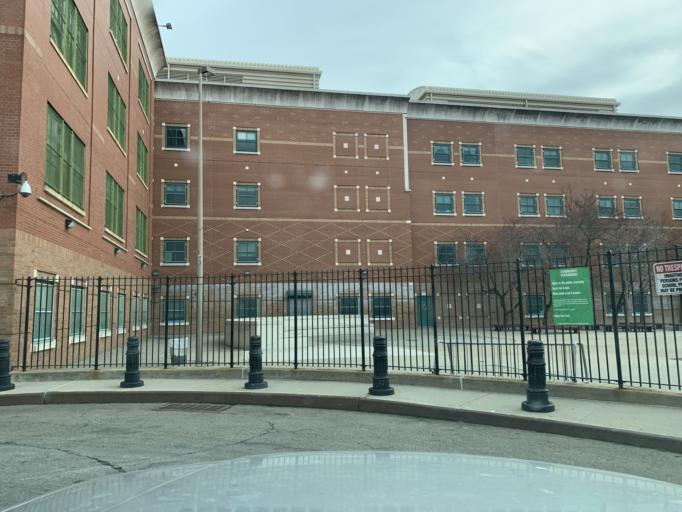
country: US
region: New York
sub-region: Queens County
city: Long Island City
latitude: 40.7373
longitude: -73.8884
